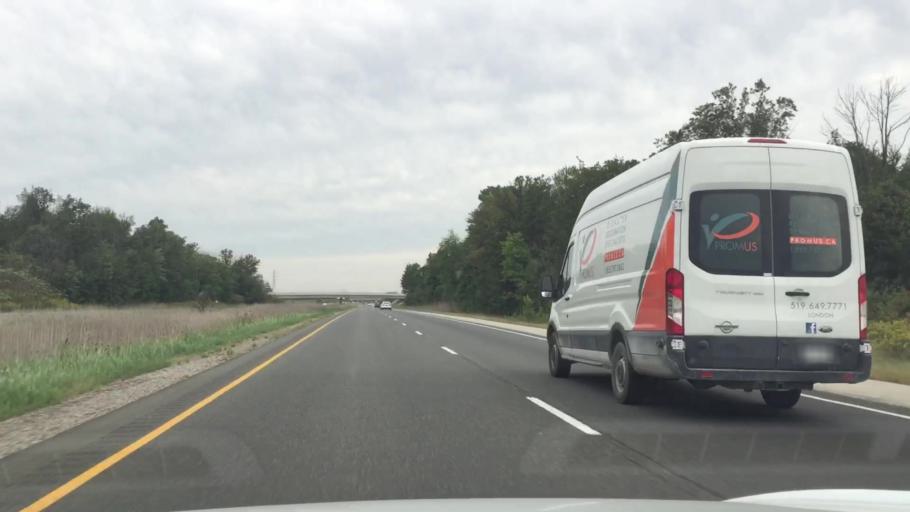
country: CA
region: Ontario
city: Delaware
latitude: 42.8860
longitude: -81.3434
